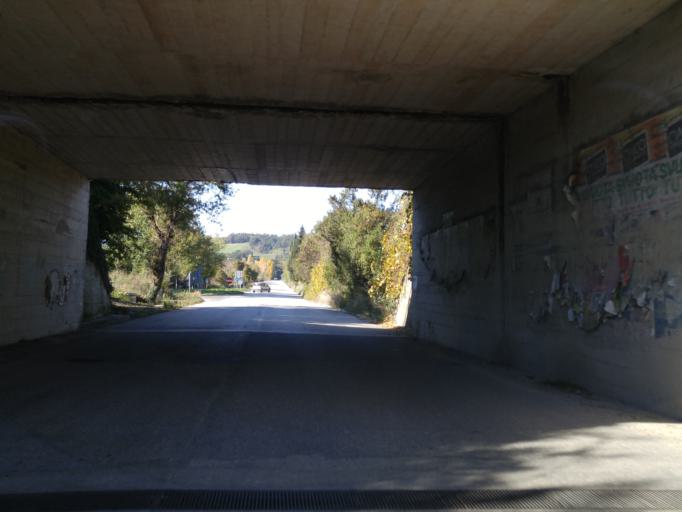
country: IT
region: The Marches
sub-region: Provincia di Pesaro e Urbino
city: Tavernelle
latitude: 43.7261
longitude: 12.8928
